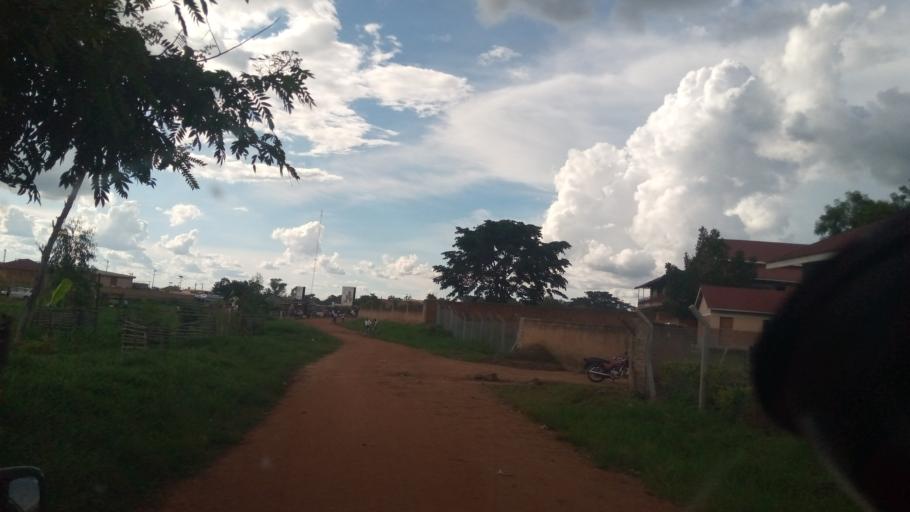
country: UG
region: Northern Region
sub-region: Lira District
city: Lira
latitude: 2.2418
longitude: 32.9003
